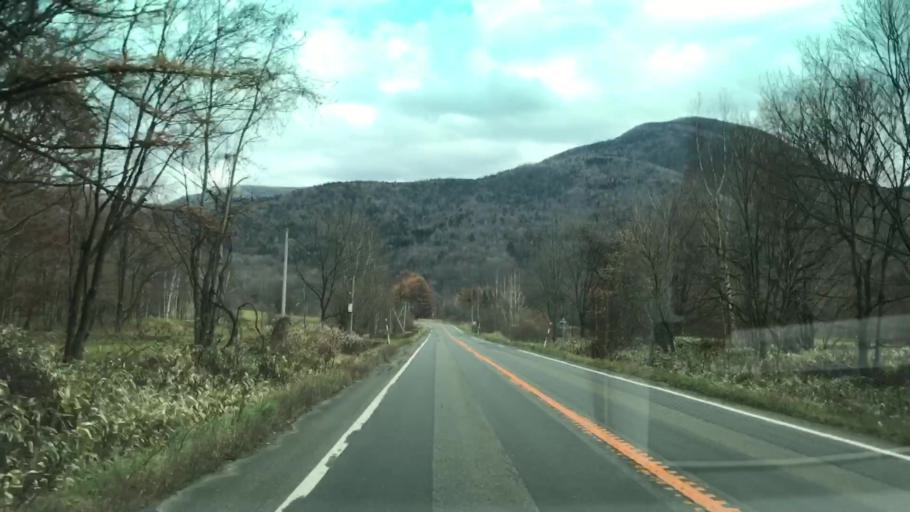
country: JP
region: Hokkaido
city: Shizunai-furukawacho
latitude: 42.8122
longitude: 142.4104
